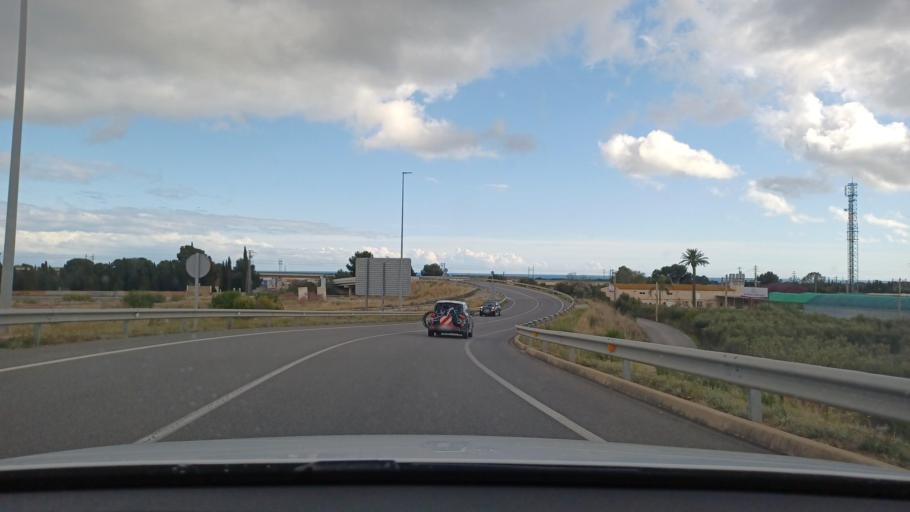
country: ES
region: Catalonia
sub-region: Provincia de Tarragona
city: Cambrils
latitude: 41.0828
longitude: 1.0370
